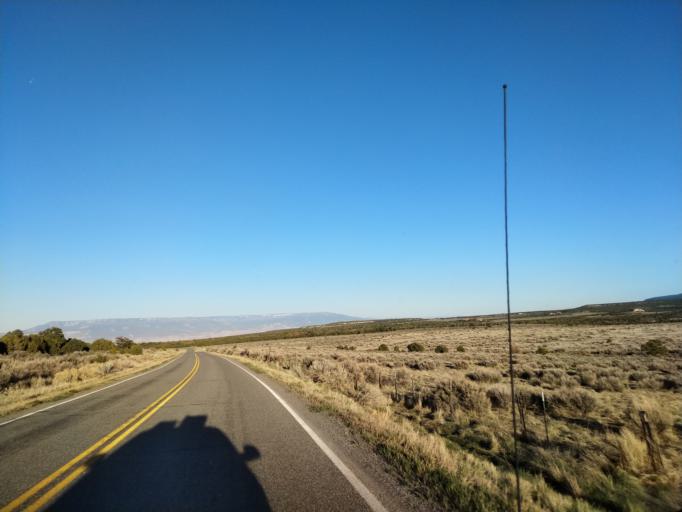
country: US
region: Colorado
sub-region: Mesa County
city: Redlands
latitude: 39.0047
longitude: -108.6992
